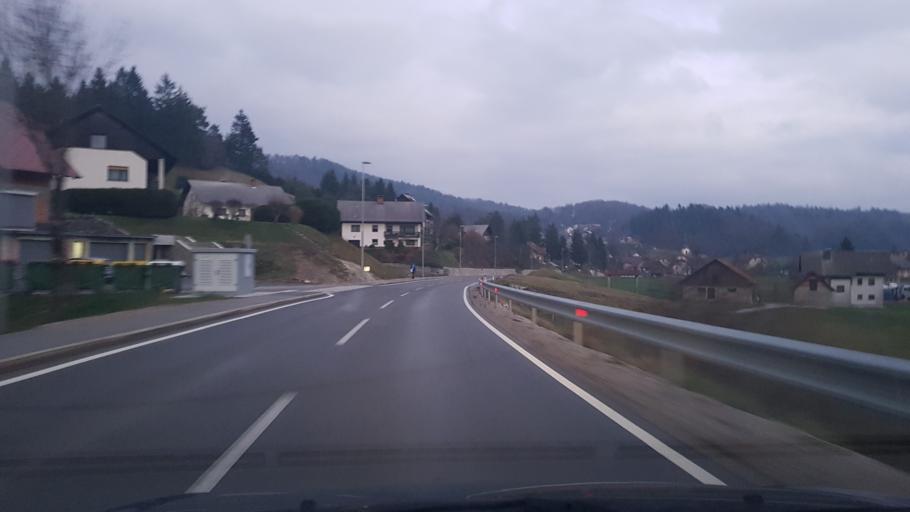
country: SI
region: Idrija
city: Idrija
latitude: 45.9576
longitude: 14.0854
